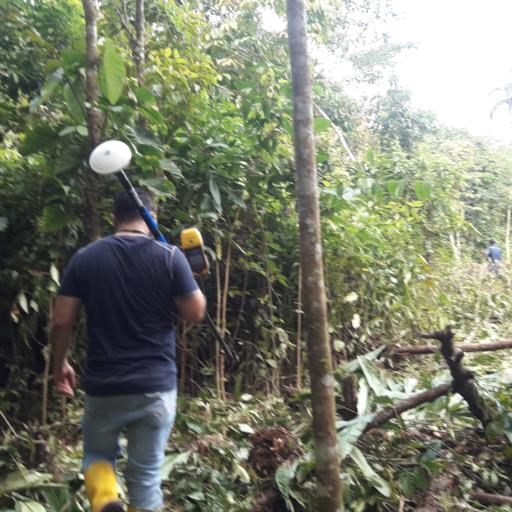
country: EC
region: Napo
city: Tena
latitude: -0.9521
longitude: -77.8611
